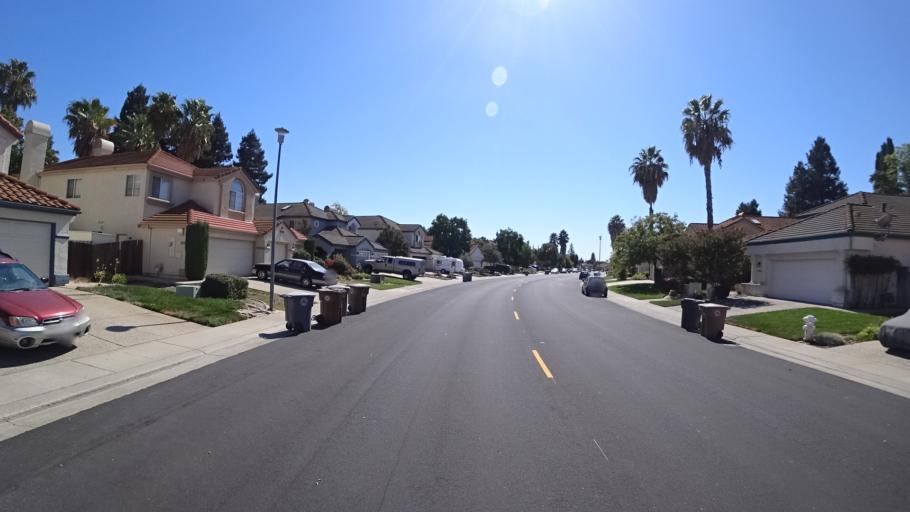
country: US
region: California
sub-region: Sacramento County
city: Laguna
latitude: 38.4295
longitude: -121.4322
